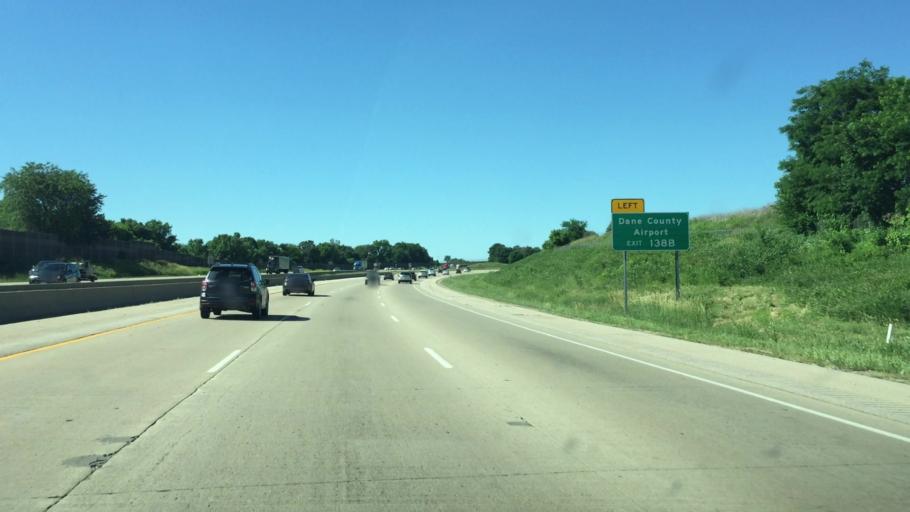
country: US
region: Wisconsin
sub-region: Dane County
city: Monona
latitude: 43.0912
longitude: -89.2849
